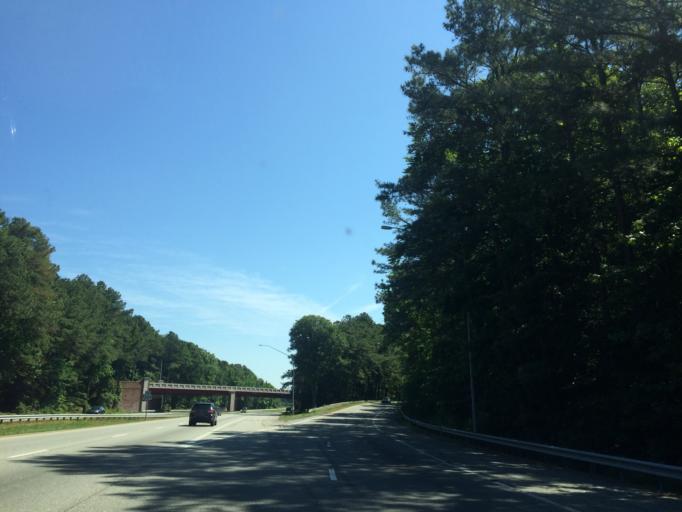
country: US
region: Maryland
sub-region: Queen Anne's County
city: Grasonville
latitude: 38.9798
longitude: -76.1700
